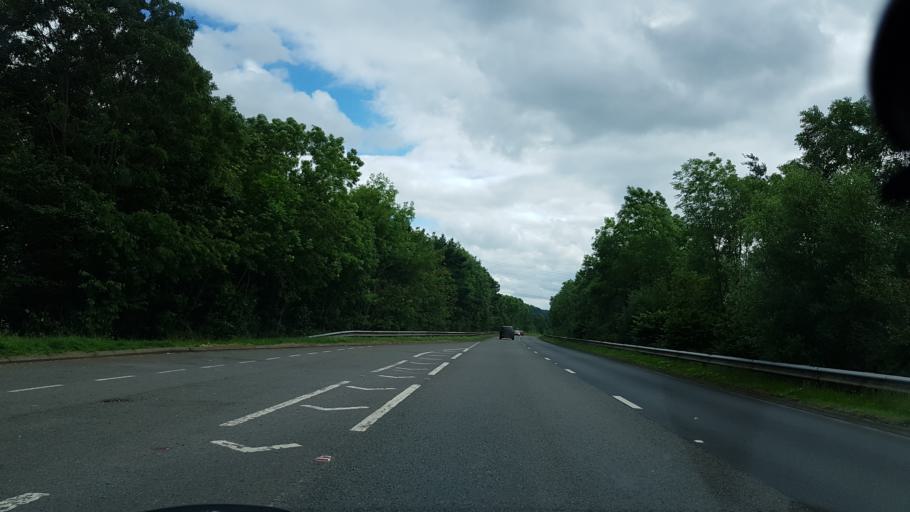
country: GB
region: Wales
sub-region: Monmouthshire
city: Abergavenny
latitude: 51.8427
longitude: -2.9995
